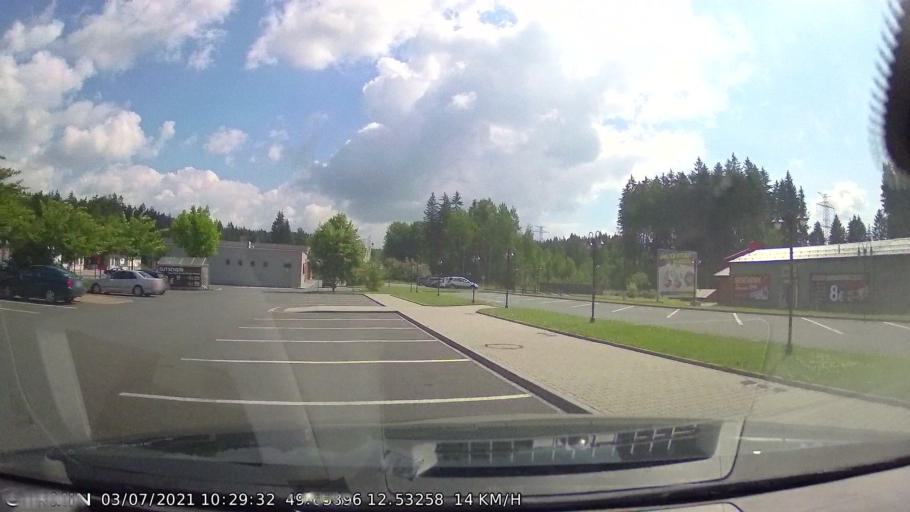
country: DE
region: Bavaria
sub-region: Upper Palatinate
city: Waidhaus
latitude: 49.6583
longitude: 12.5316
